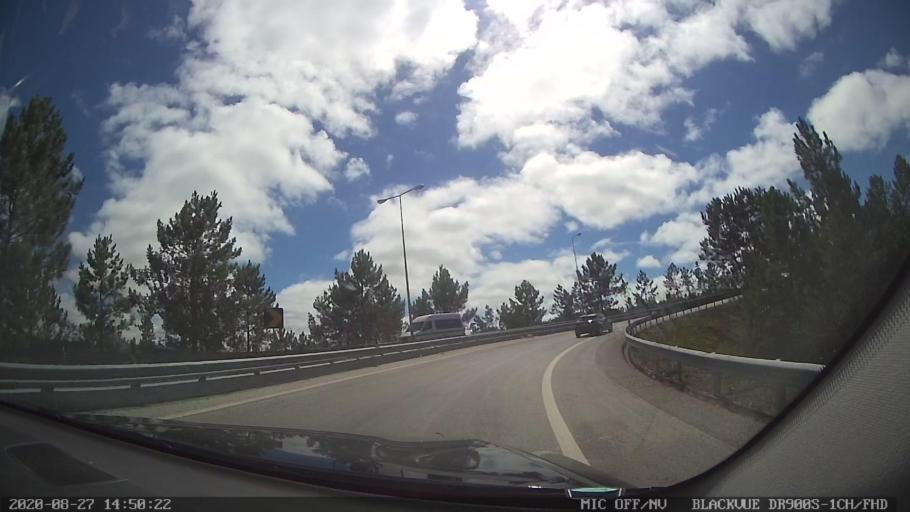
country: PT
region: Leiria
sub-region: Leiria
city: Maceira
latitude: 39.7422
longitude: -8.8704
